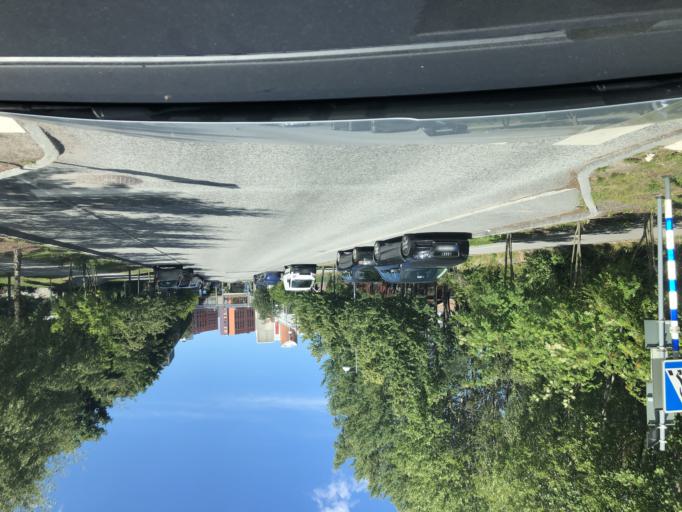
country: SE
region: Stockholm
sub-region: Botkyrka Kommun
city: Tullinge
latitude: 59.2206
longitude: 17.9319
